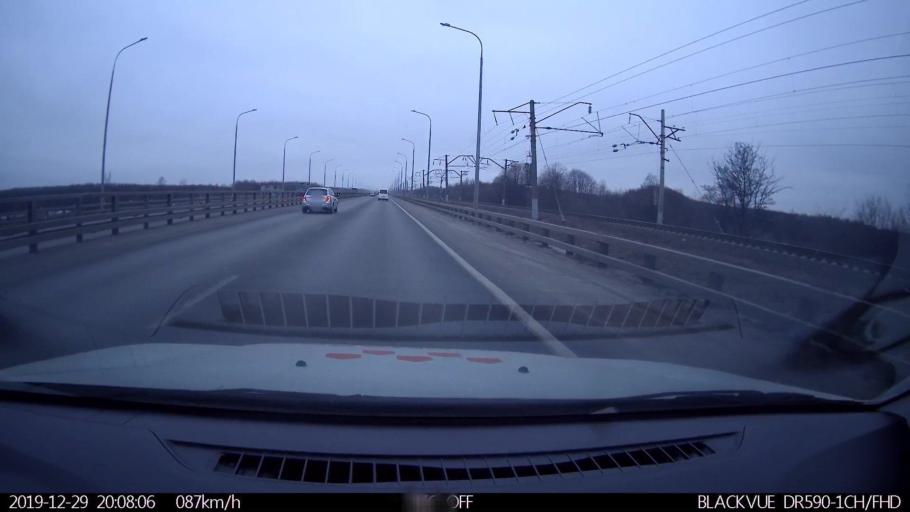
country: RU
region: Nizjnij Novgorod
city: Neklyudovo
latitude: 56.3889
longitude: 43.9711
